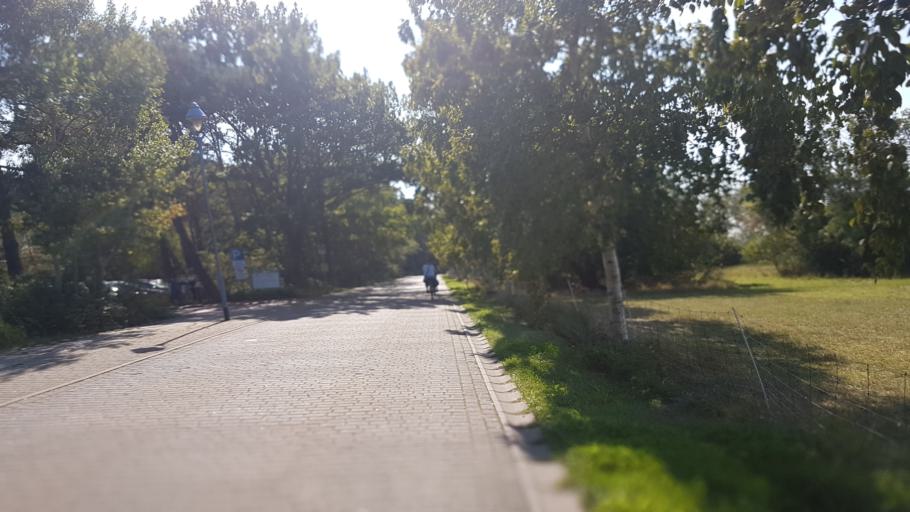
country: DE
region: Mecklenburg-Vorpommern
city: Ostseebad Gohren
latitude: 54.3300
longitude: 13.7293
